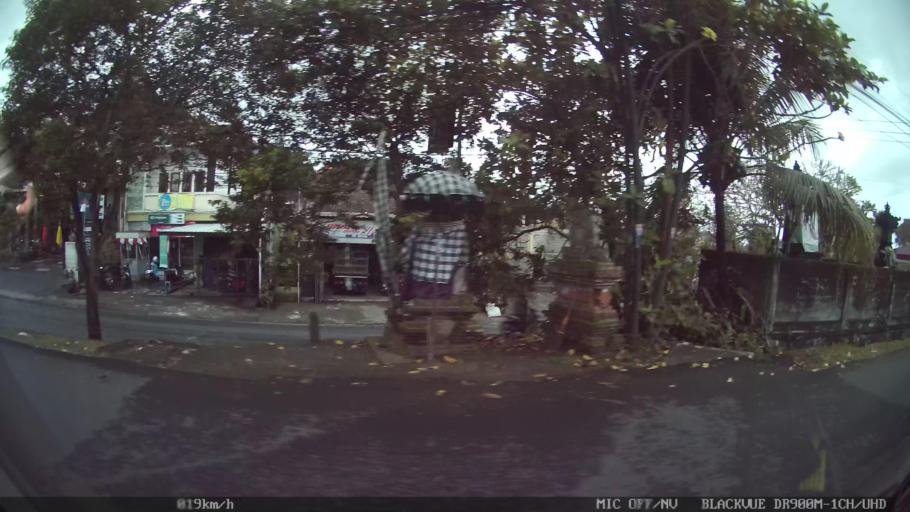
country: ID
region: Bali
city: Banjar Mambalkajanan
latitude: -8.5440
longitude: 115.2142
